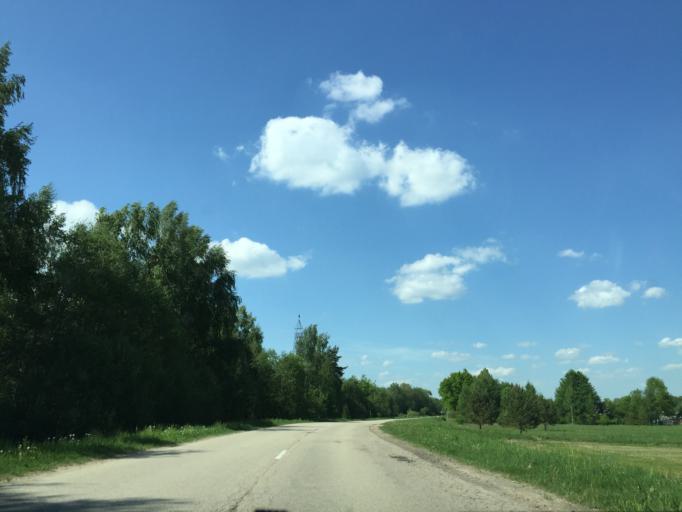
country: LV
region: Ozolnieku
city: Ozolnieki
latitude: 56.6215
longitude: 23.9327
